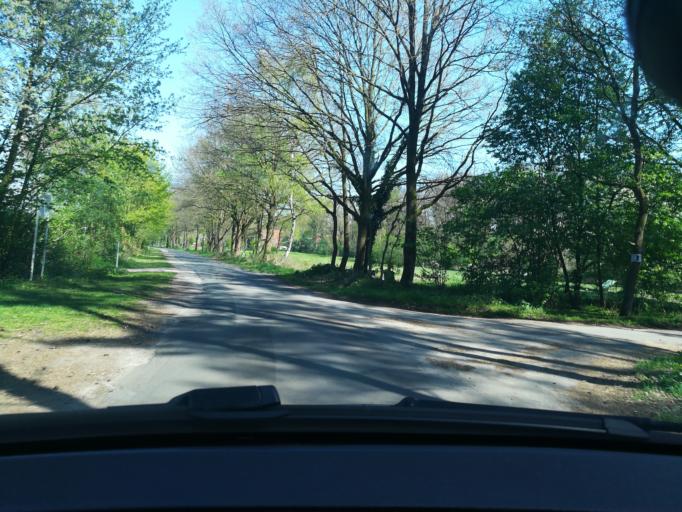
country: DE
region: North Rhine-Westphalia
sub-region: Regierungsbezirk Munster
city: Sassenberg
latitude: 52.0151
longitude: 8.0965
